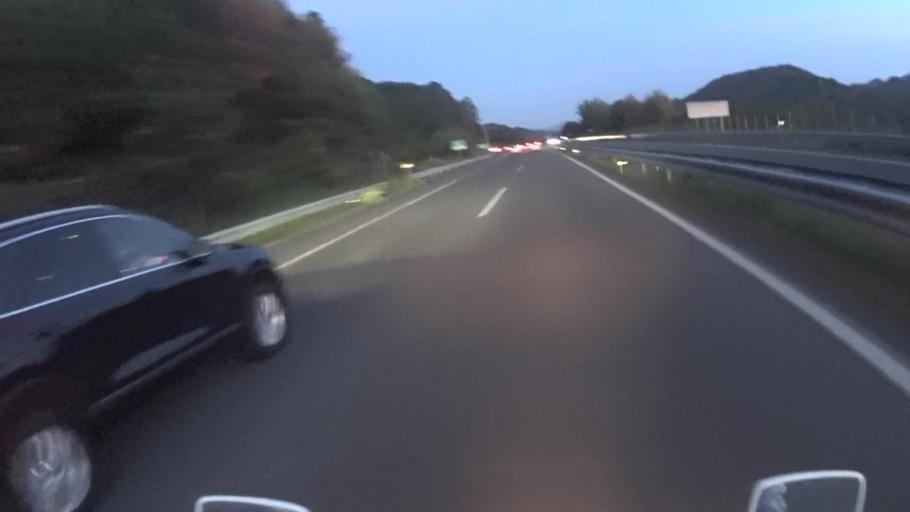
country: JP
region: Kyoto
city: Kameoka
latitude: 35.1257
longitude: 135.4773
